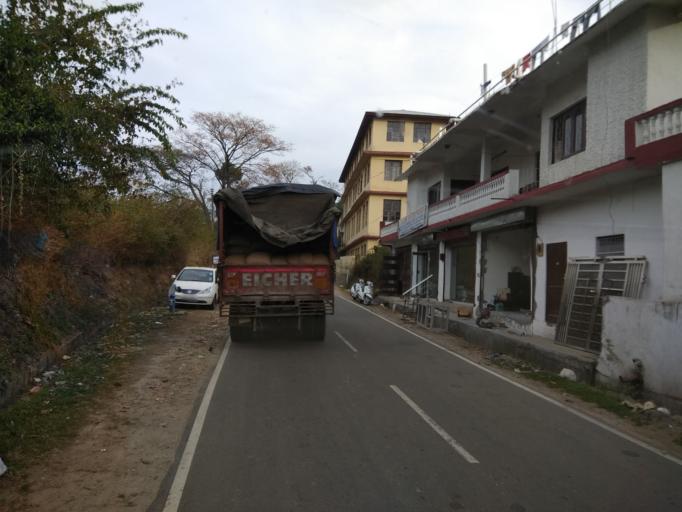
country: IN
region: Himachal Pradesh
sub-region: Kangra
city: Palampur
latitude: 32.1147
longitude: 76.5155
